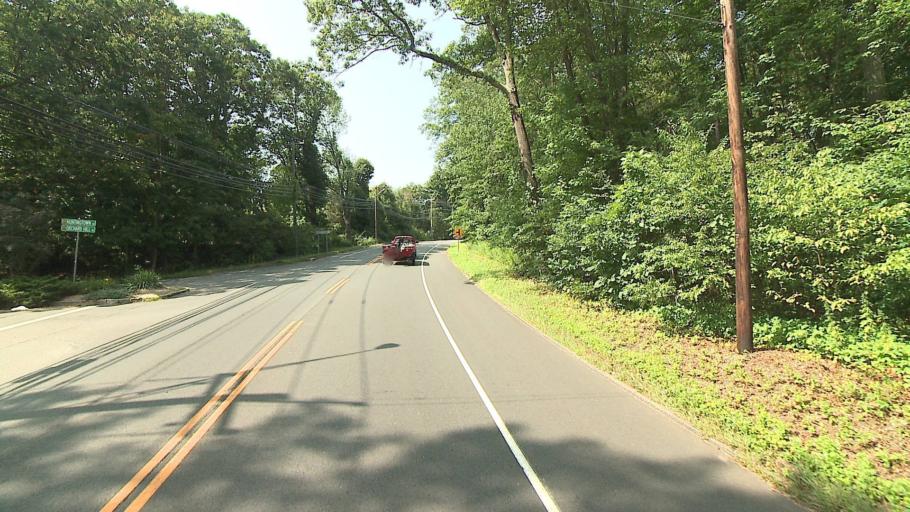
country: US
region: Connecticut
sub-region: Fairfield County
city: Newtown
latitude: 41.3808
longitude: -73.2832
